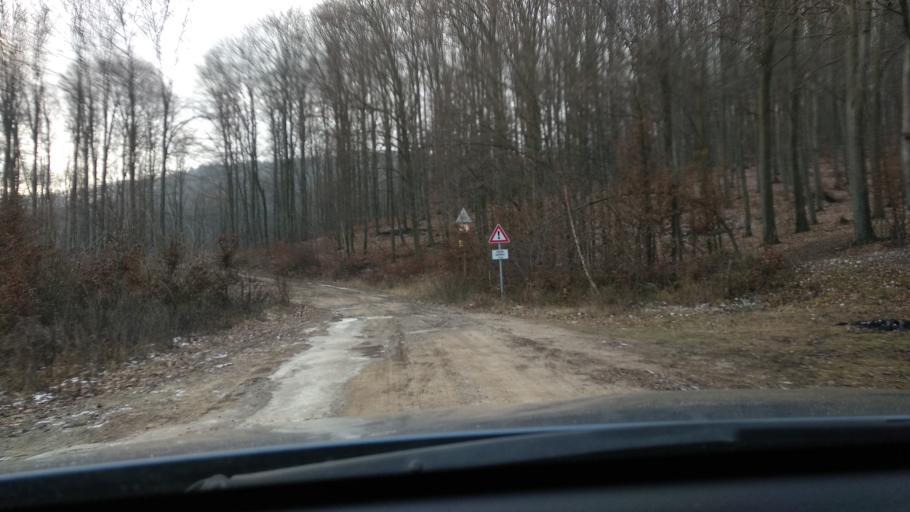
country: SK
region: Trenciansky
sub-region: Okres Trencin
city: Trencin
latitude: 48.8006
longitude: 18.0748
